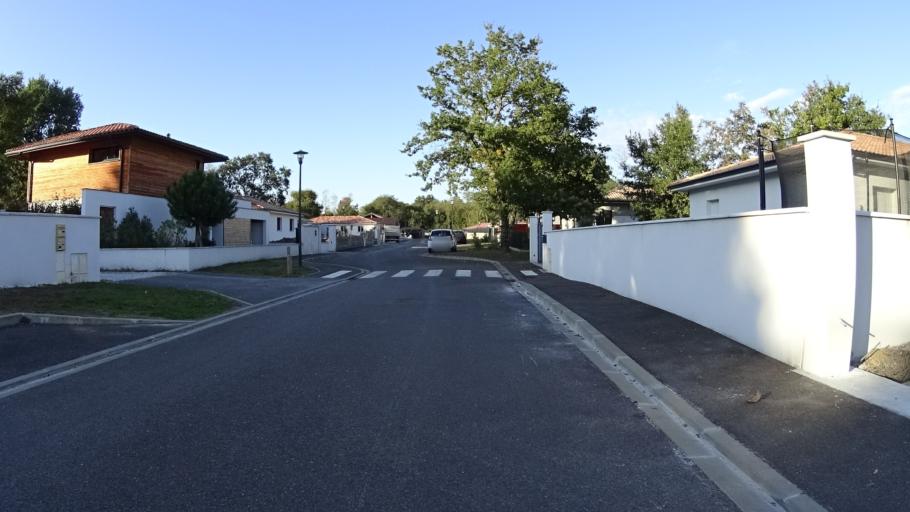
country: FR
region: Aquitaine
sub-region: Departement des Landes
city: Saint-Paul-les-Dax
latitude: 43.7404
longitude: -1.0468
